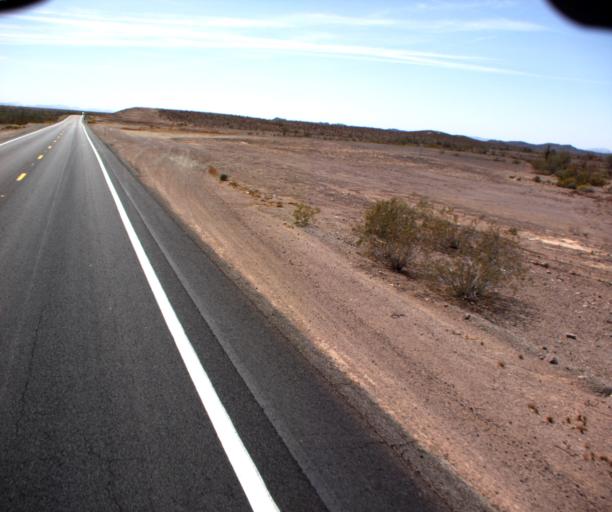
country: US
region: Arizona
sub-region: La Paz County
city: Quartzsite
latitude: 33.1787
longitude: -114.2758
